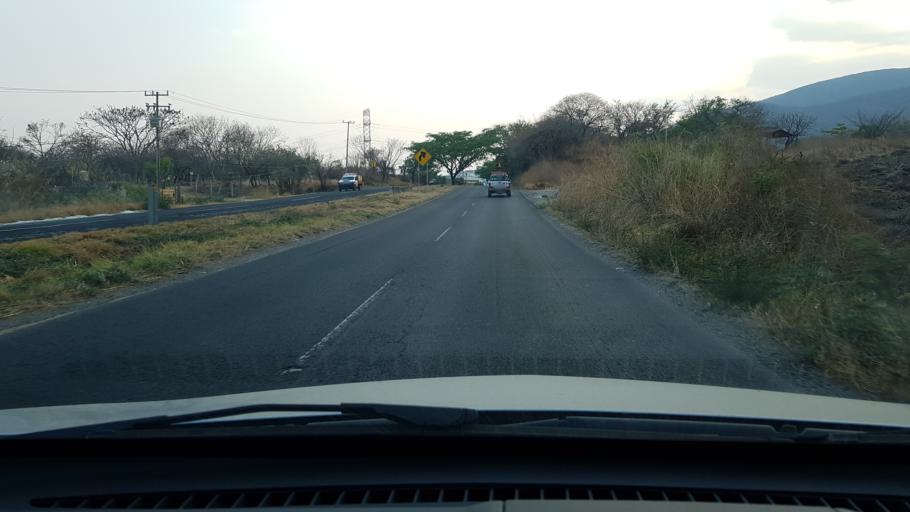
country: MX
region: Morelos
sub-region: Jiutepec
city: Independencia
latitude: 18.8620
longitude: -99.0965
